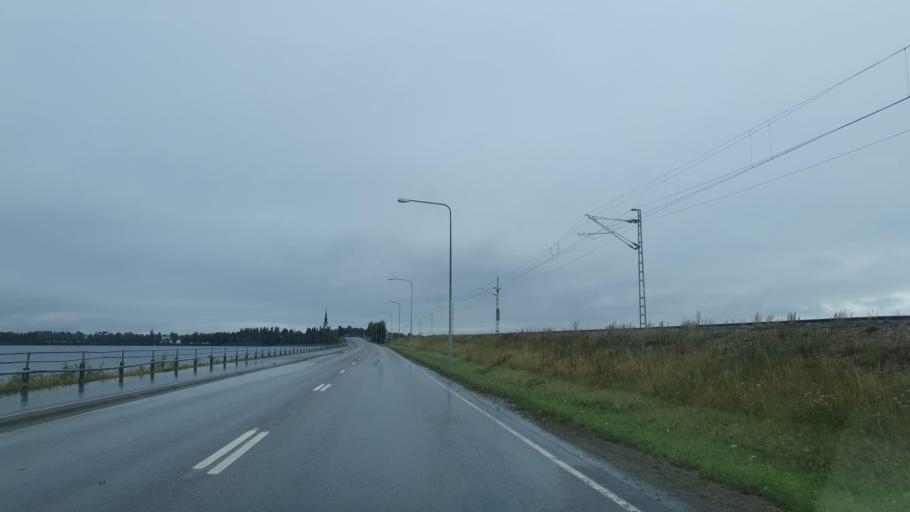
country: FI
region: Lapland
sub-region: Itae-Lappi
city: Kemijaervi
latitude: 66.7159
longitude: 27.4642
